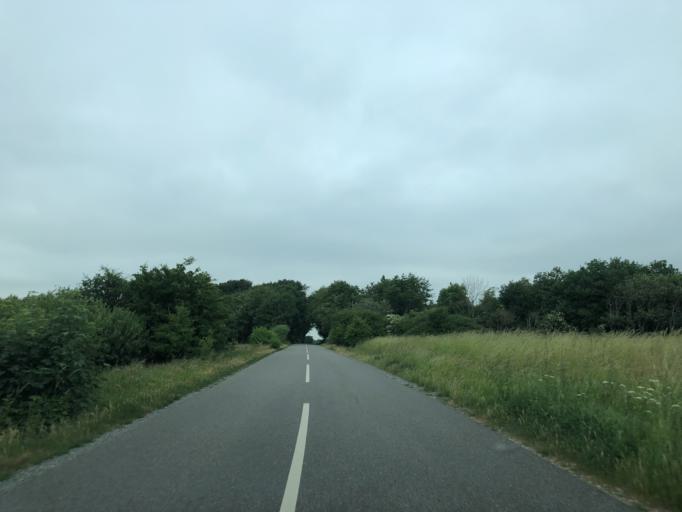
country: DK
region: Central Jutland
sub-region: Holstebro Kommune
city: Holstebro
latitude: 56.2414
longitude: 8.6209
